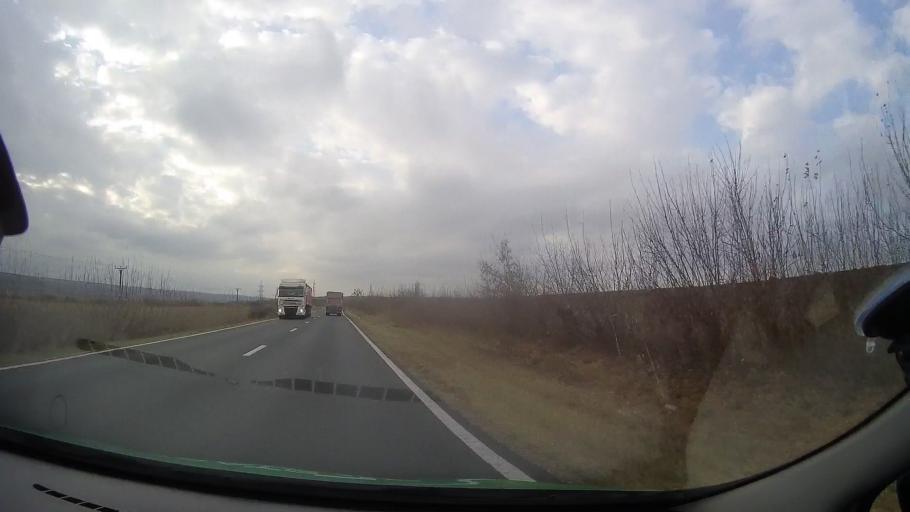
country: RO
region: Constanta
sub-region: Comuna Mircea Voda
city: Satu Nou
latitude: 44.2705
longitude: 28.2069
